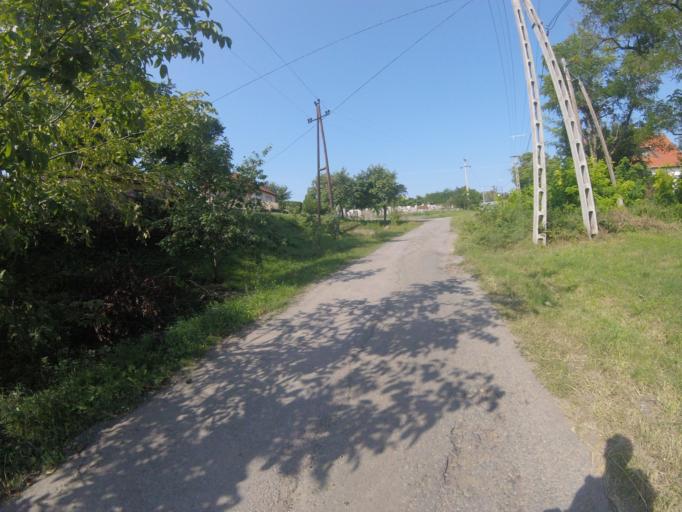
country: HU
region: Nograd
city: Bujak
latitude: 47.8823
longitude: 19.5383
